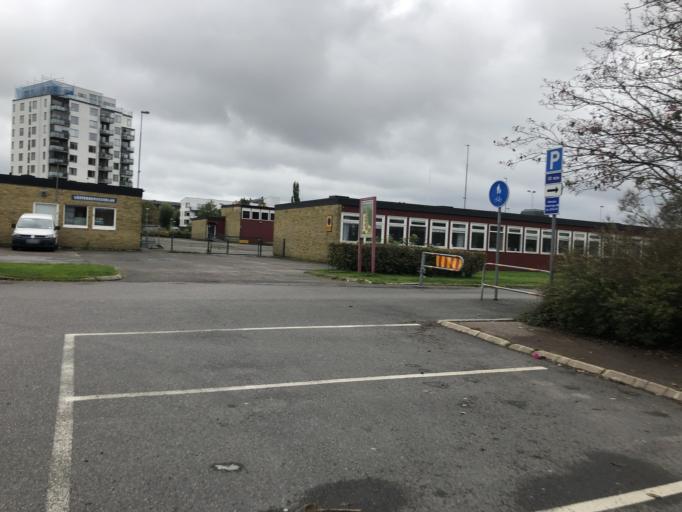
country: SE
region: Vaestra Goetaland
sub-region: Molndal
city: Moelndal
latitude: 57.6618
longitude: 11.9906
